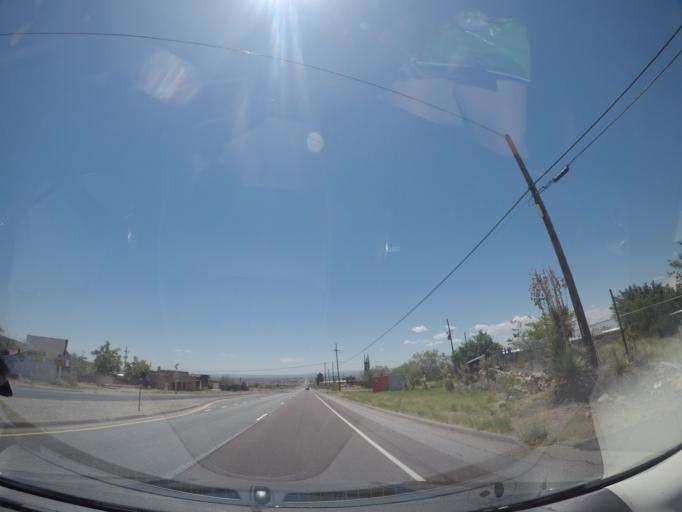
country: US
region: New Mexico
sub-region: Dona Ana County
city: White Sands
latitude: 32.4256
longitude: -106.5981
